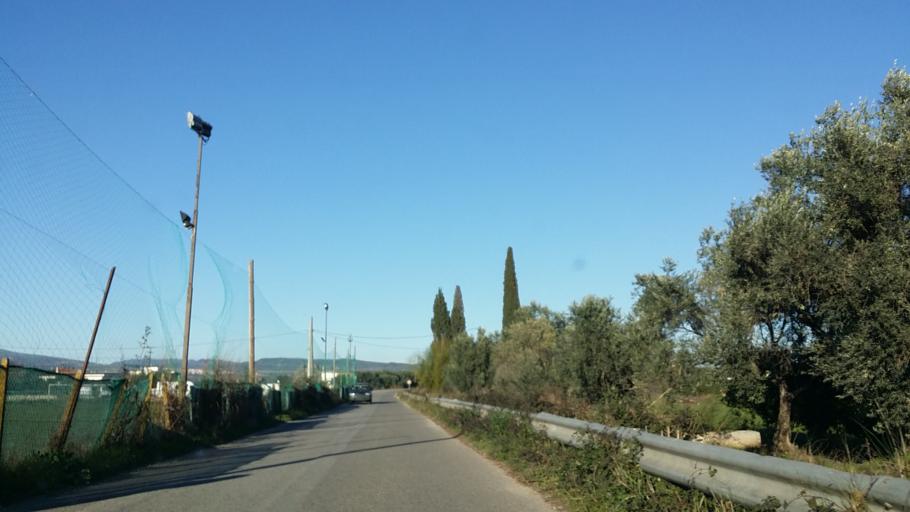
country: GR
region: West Greece
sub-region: Nomos Aitolias kai Akarnanias
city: Lepenou
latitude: 38.6564
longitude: 21.2890
